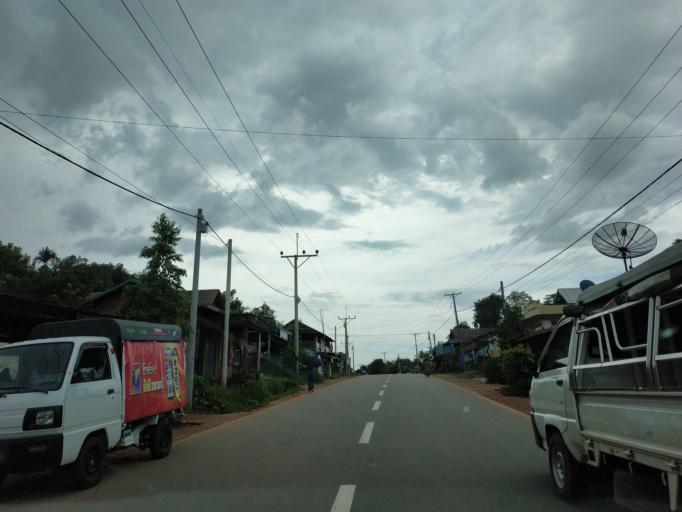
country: MM
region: Tanintharyi
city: Dawei
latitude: 13.9114
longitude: 98.2503
